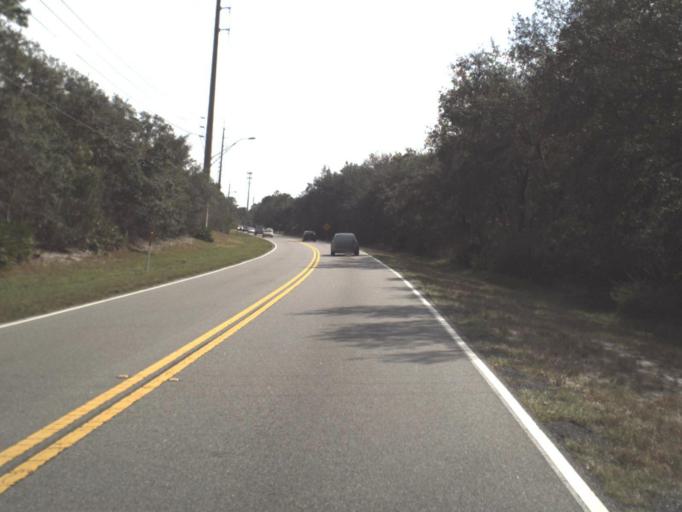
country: US
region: Florida
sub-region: Osceola County
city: Poinciana
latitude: 28.1882
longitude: -81.4641
